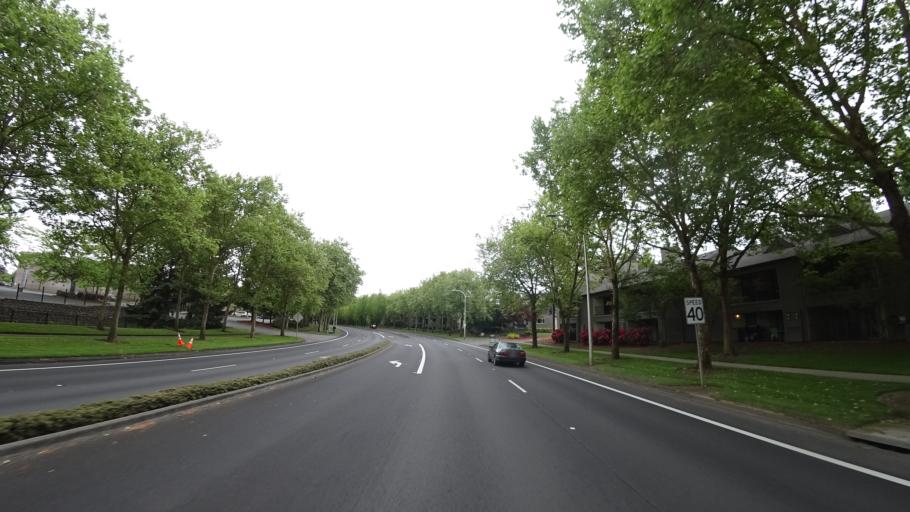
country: US
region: Oregon
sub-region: Washington County
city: Rockcreek
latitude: 45.5399
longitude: -122.8737
